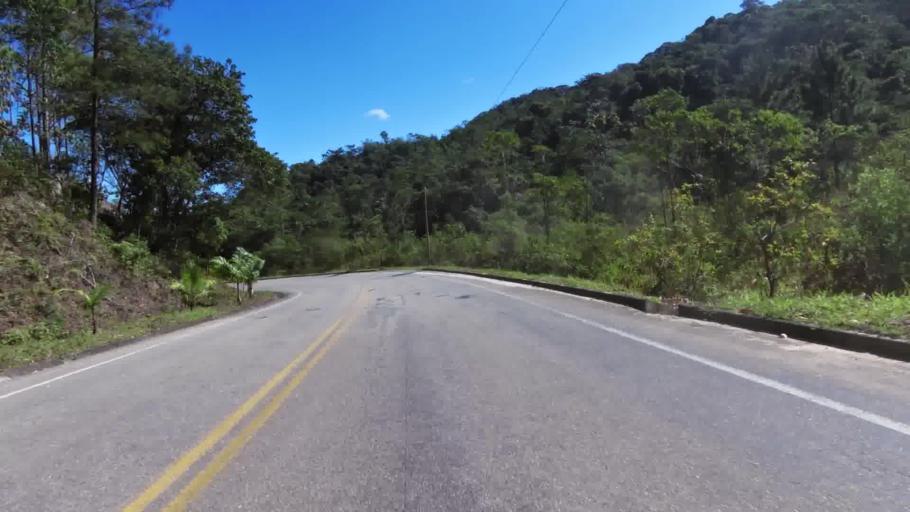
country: BR
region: Espirito Santo
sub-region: Vargem Alta
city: Vargem Alta
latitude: -20.6854
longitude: -40.9449
